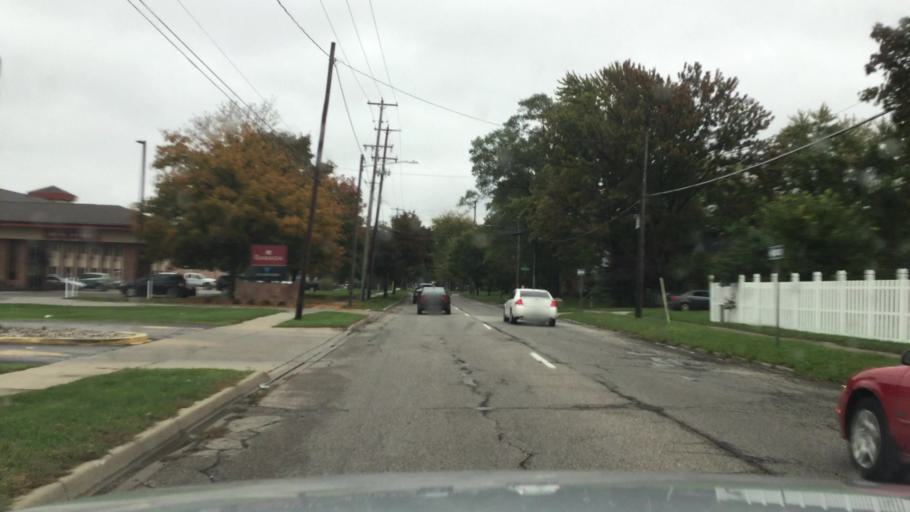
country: US
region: Michigan
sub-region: Saginaw County
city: Saginaw
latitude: 43.4367
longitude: -83.9891
